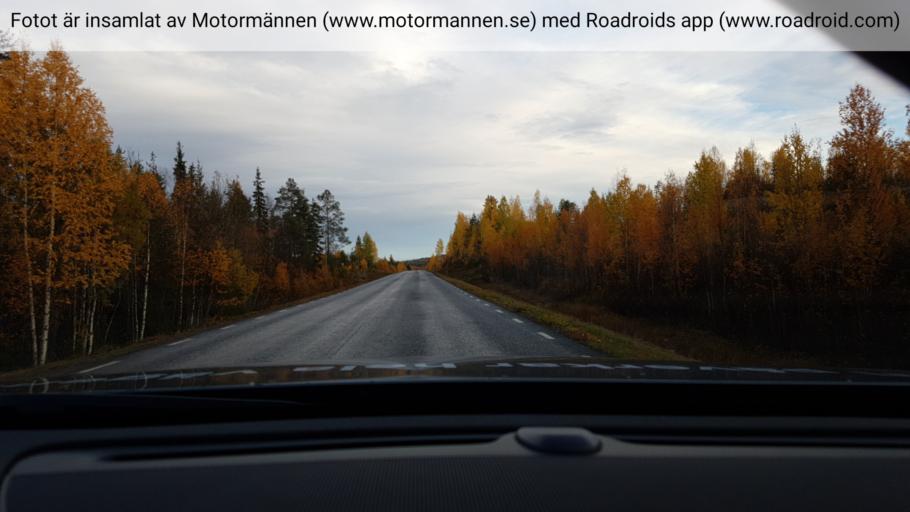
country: SE
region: Norrbotten
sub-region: Overkalix Kommun
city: OEverkalix
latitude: 66.9174
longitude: 22.7580
